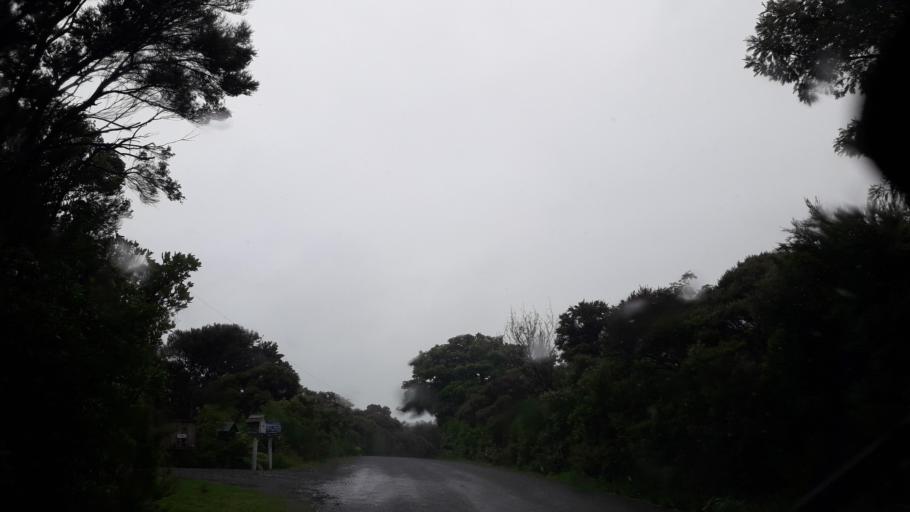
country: NZ
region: Northland
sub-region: Far North District
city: Paihia
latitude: -35.2305
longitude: 174.2613
